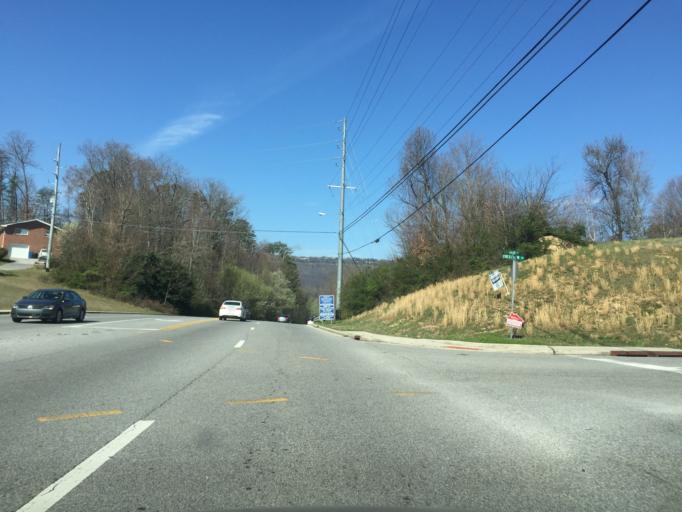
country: US
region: Tennessee
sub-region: Hamilton County
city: Red Bank
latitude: 35.1192
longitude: -85.2815
